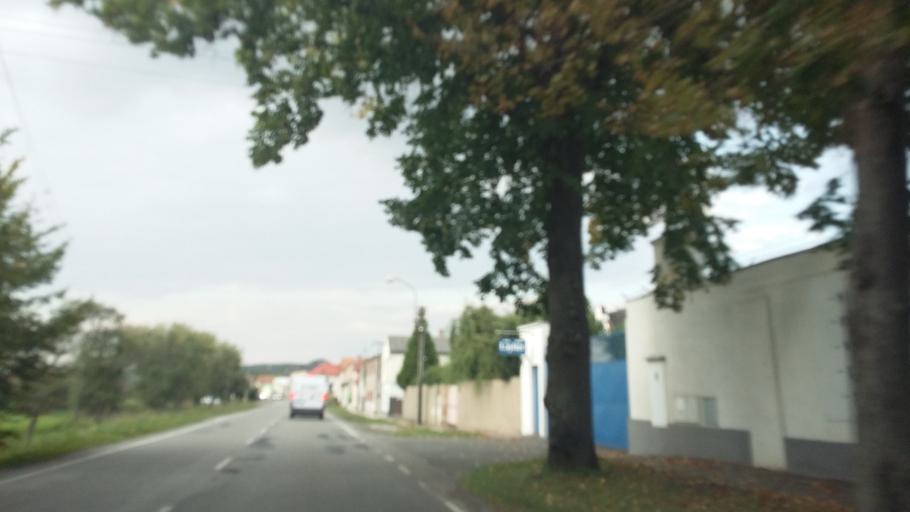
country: CZ
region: Central Bohemia
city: Benatky nad Jizerou
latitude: 50.3254
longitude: 14.8655
